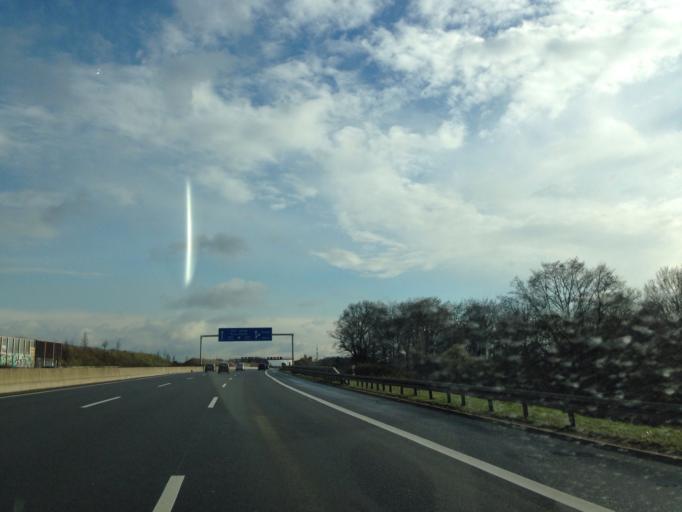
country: DE
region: North Rhine-Westphalia
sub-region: Regierungsbezirk Dusseldorf
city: Meerbusch
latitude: 51.2735
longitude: 6.6430
